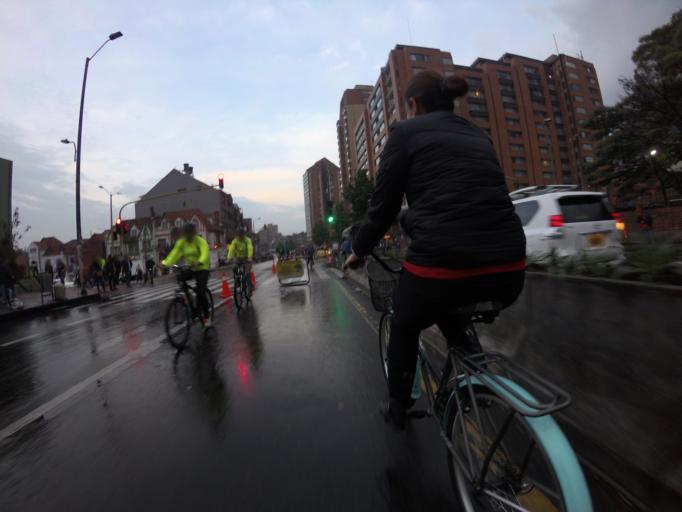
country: CO
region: Bogota D.C.
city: Bogota
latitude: 4.6311
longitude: -74.0643
